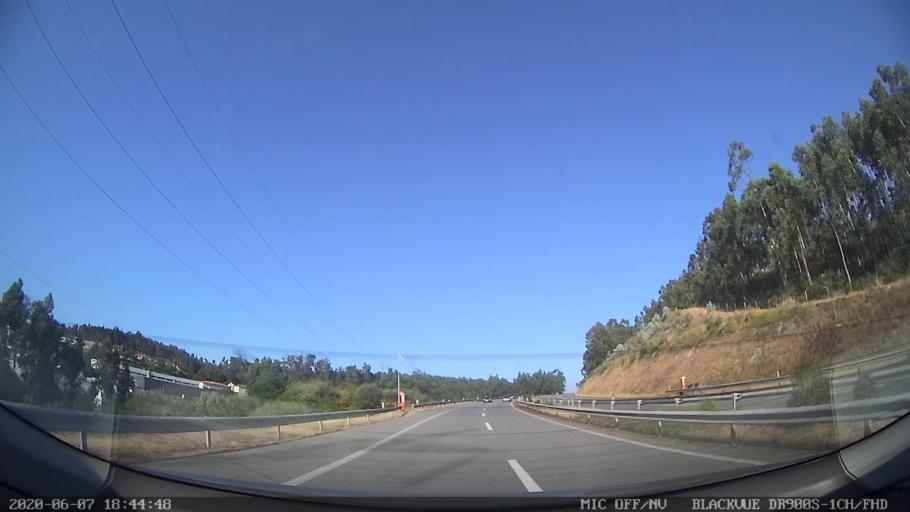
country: PT
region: Braga
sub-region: Vila Nova de Famalicao
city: Joane
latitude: 41.4076
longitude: -8.4238
